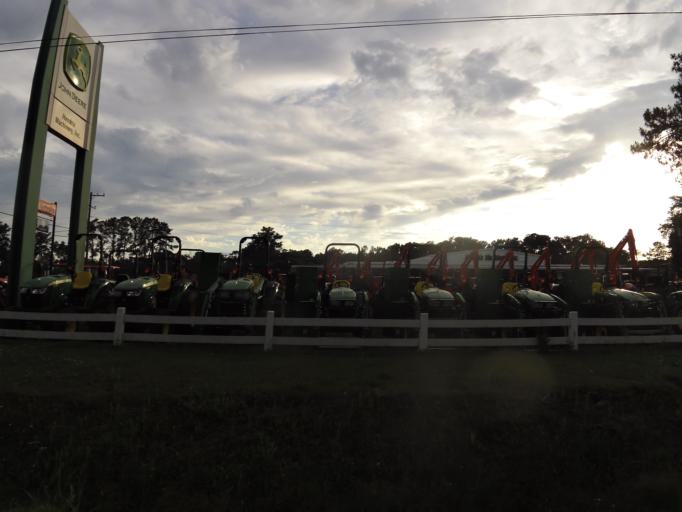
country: US
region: Georgia
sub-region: Chatham County
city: Garden City
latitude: 32.0906
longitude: -81.1997
